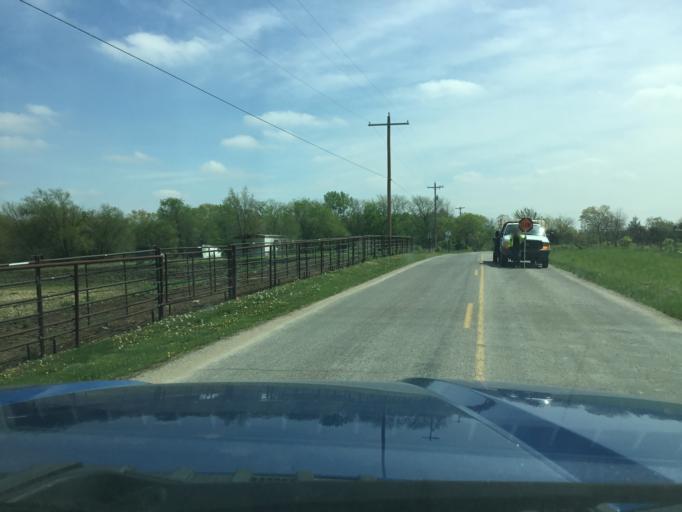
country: US
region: Kansas
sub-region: Shawnee County
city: Topeka
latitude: 39.1170
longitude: -95.5778
